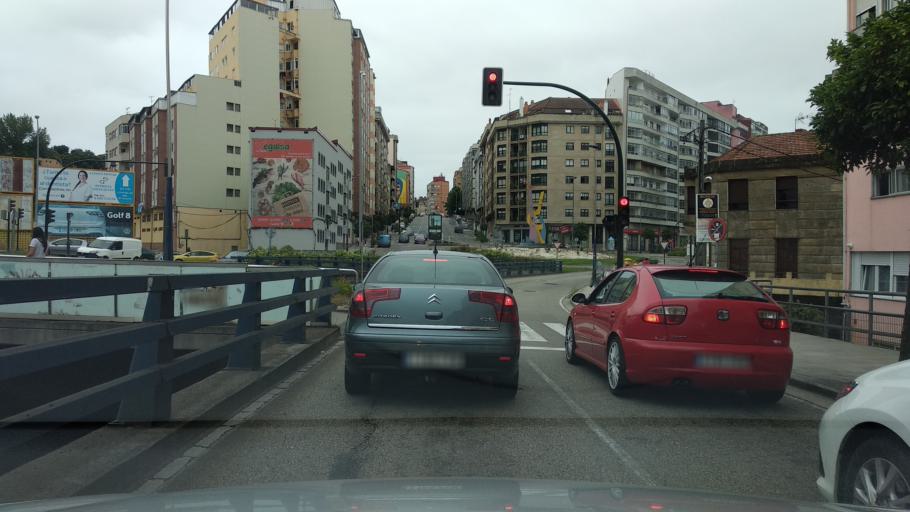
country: ES
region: Galicia
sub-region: Provincia de Pontevedra
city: Vigo
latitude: 42.2430
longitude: -8.6972
